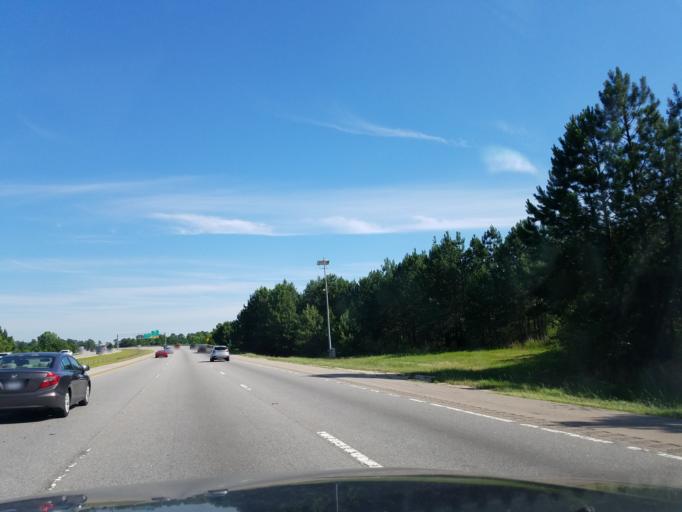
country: US
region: North Carolina
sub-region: Wake County
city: Raleigh
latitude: 35.8830
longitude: -78.5906
